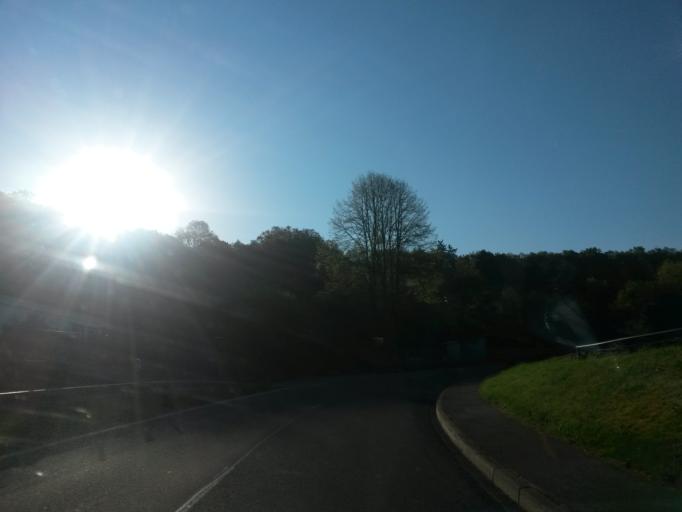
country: DE
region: North Rhine-Westphalia
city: Wiehl
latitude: 50.9542
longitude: 7.5079
